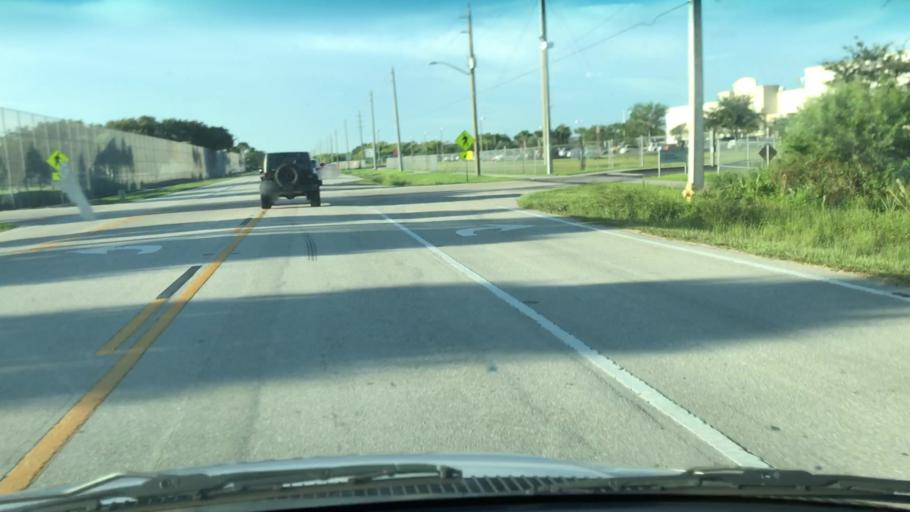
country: US
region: Florida
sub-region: Lee County
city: Villas
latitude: 26.5394
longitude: -81.8470
